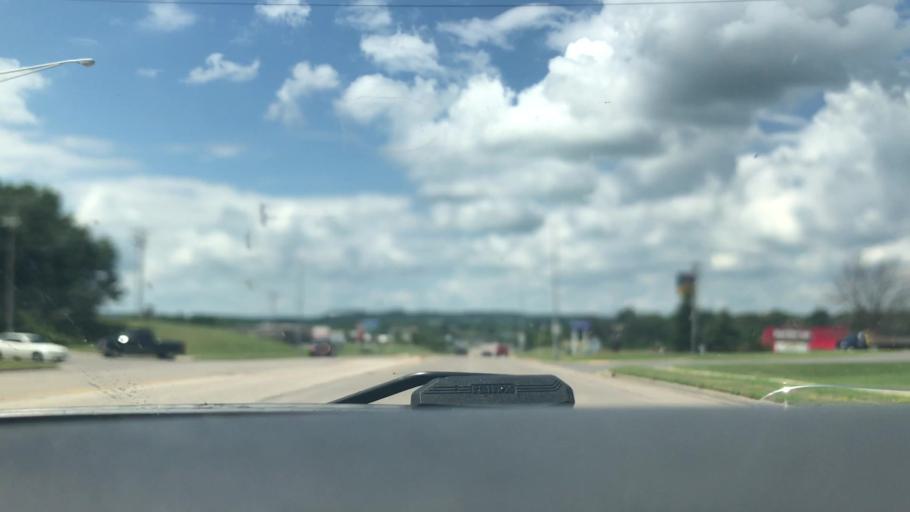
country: US
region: Wisconsin
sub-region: Jackson County
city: Black River Falls
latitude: 44.2944
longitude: -90.8307
